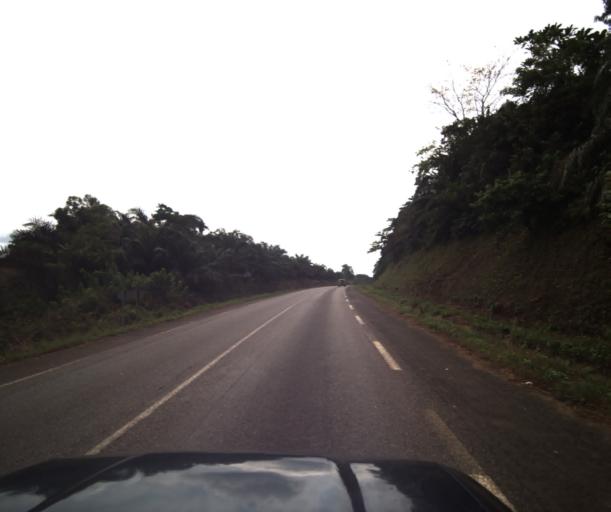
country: CM
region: Littoral
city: Edea
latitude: 3.8386
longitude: 10.4538
